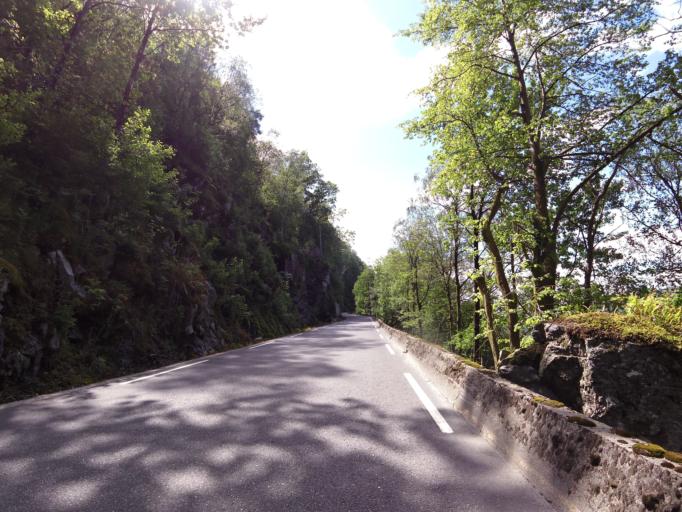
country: NO
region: Vest-Agder
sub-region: Kvinesdal
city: Liknes
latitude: 58.2965
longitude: 6.9481
